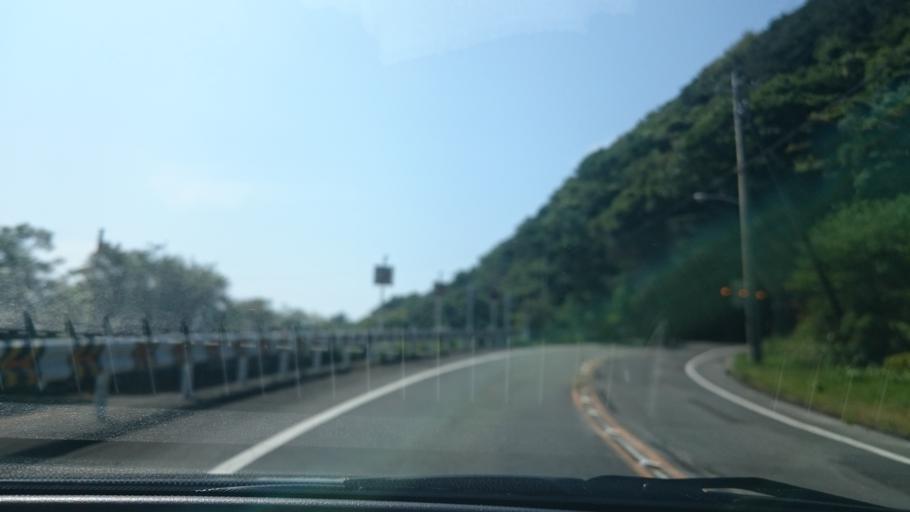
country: JP
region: Shizuoka
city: Heda
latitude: 34.8618
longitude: 138.7691
